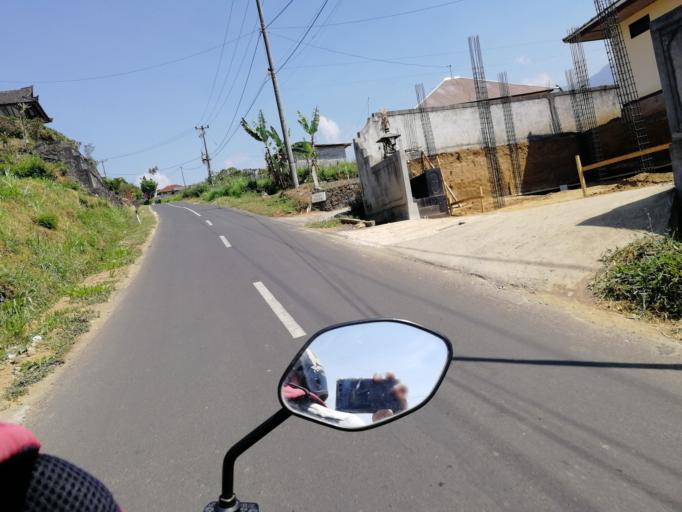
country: ID
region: Bali
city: Peneng
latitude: -8.3021
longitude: 115.1820
